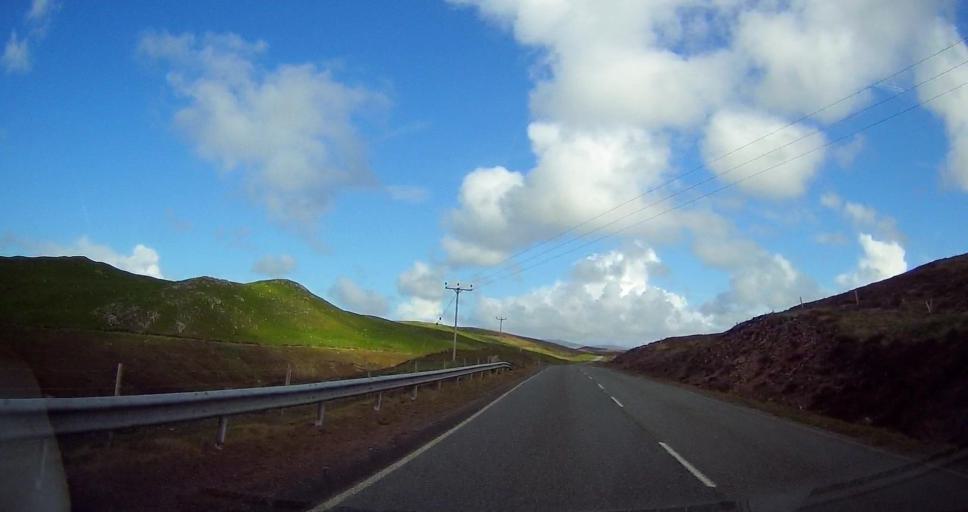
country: GB
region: Scotland
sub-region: Shetland Islands
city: Lerwick
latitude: 60.4226
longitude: -1.3949
